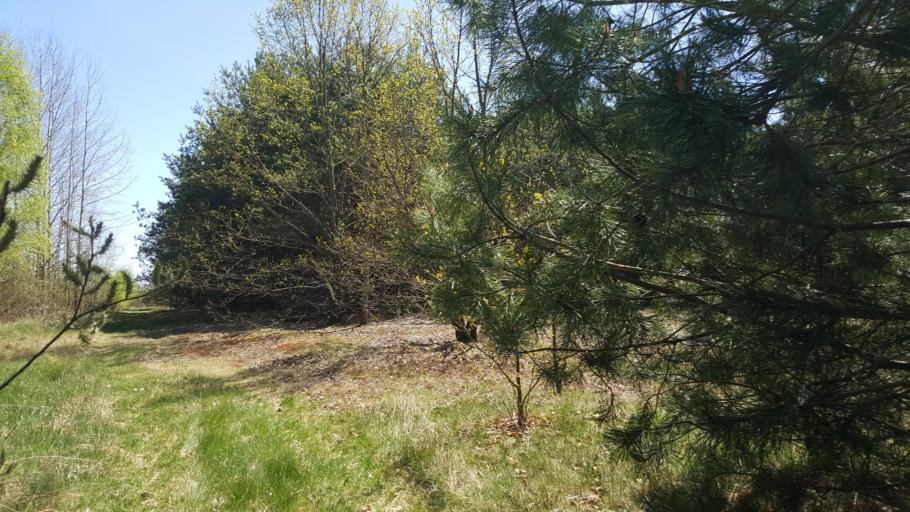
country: BY
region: Brest
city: Kamyanyets
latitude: 52.4264
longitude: 23.8537
